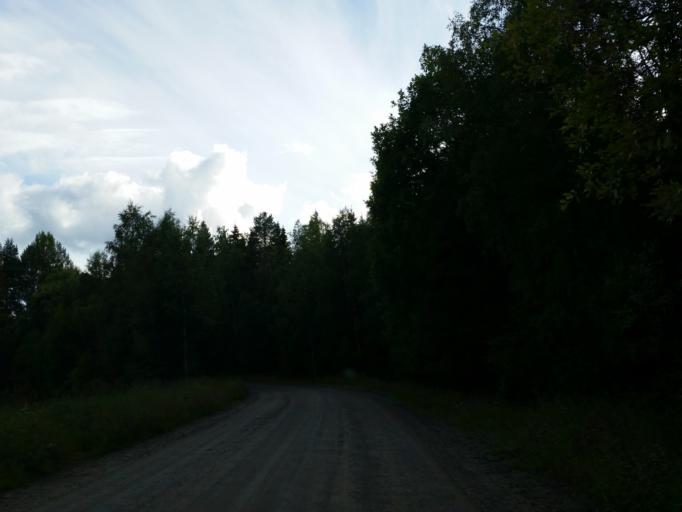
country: SE
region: Vaesterbotten
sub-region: Robertsfors Kommun
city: Robertsfors
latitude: 64.0464
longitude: 20.8513
